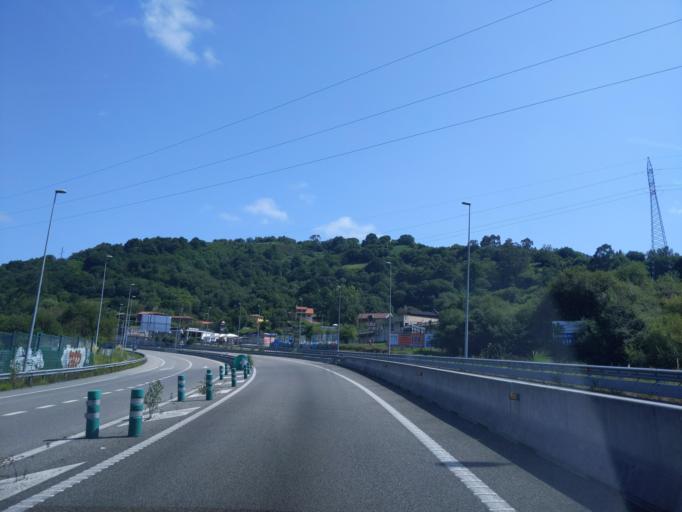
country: ES
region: Asturias
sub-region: Province of Asturias
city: Sama
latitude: 43.3261
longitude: -5.7156
